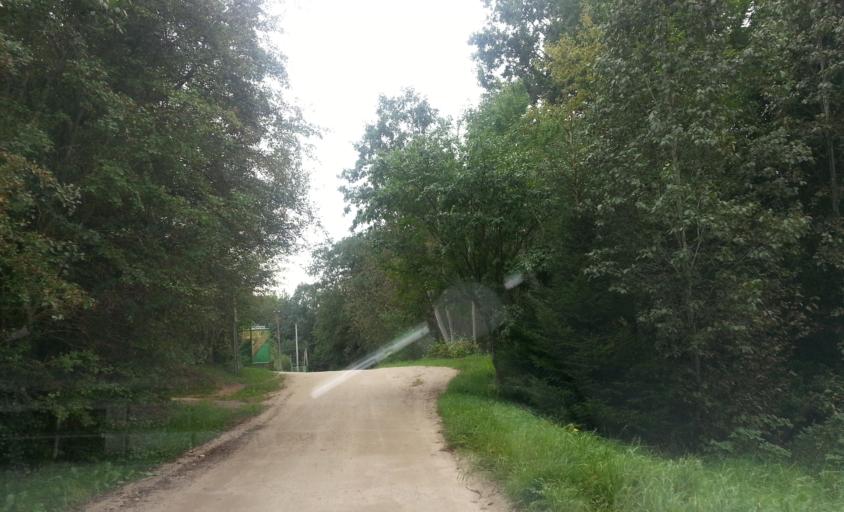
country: LT
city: Grigiskes
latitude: 54.7620
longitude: 25.0219
